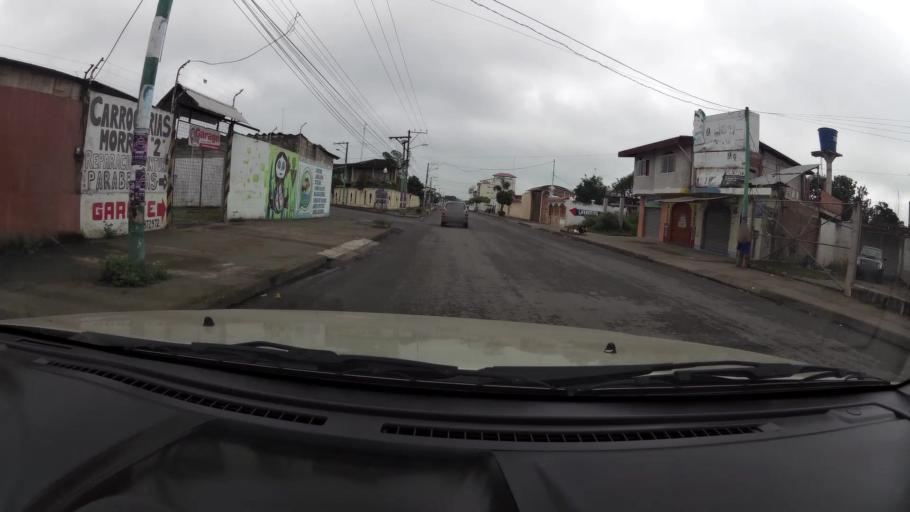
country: EC
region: El Oro
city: Pasaje
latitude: -3.3267
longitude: -79.8145
